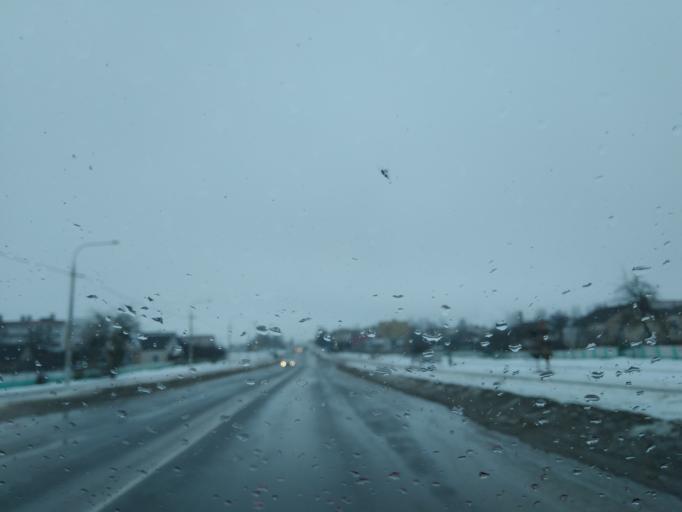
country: BY
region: Minsk
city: Nyasvizh
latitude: 53.2334
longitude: 26.6504
